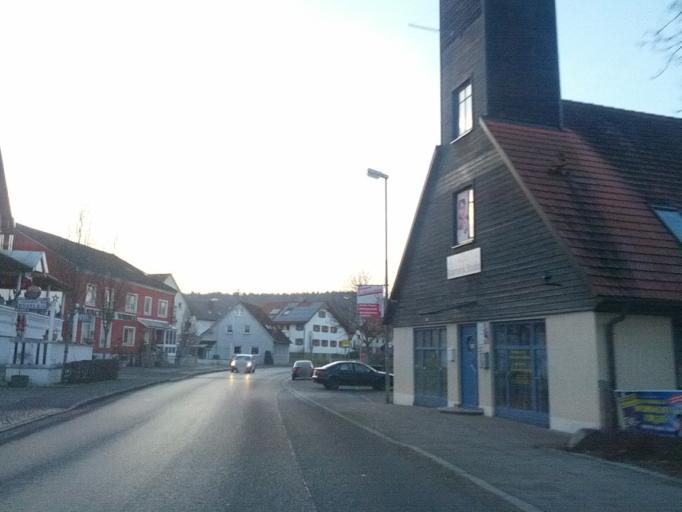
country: DE
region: Baden-Wuerttemberg
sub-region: Tuebingen Region
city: Aitrach
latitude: 47.9394
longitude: 10.0913
